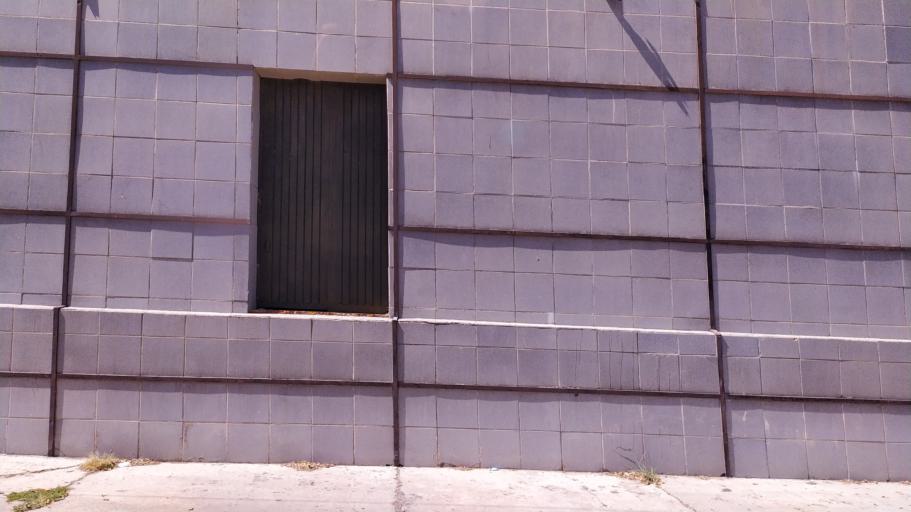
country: MX
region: Jalisco
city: Guadalajara
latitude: 20.6735
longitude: -103.3964
